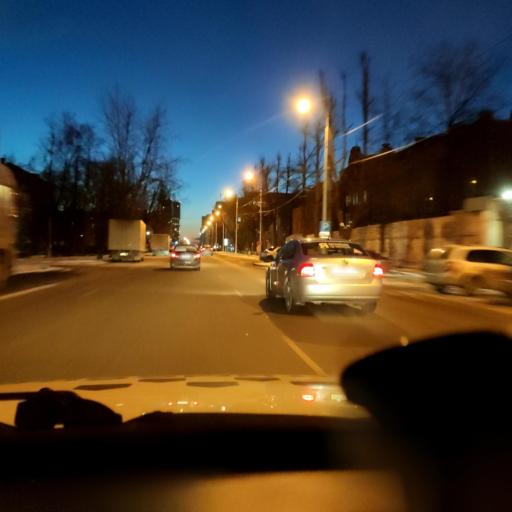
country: RU
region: Perm
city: Perm
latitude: 58.0139
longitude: 56.2145
